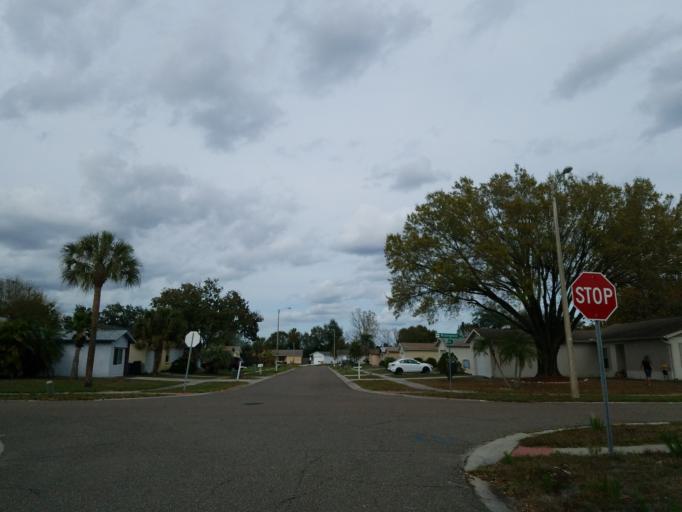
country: US
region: Florida
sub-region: Hillsborough County
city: Brandon
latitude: 27.9205
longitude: -82.3088
